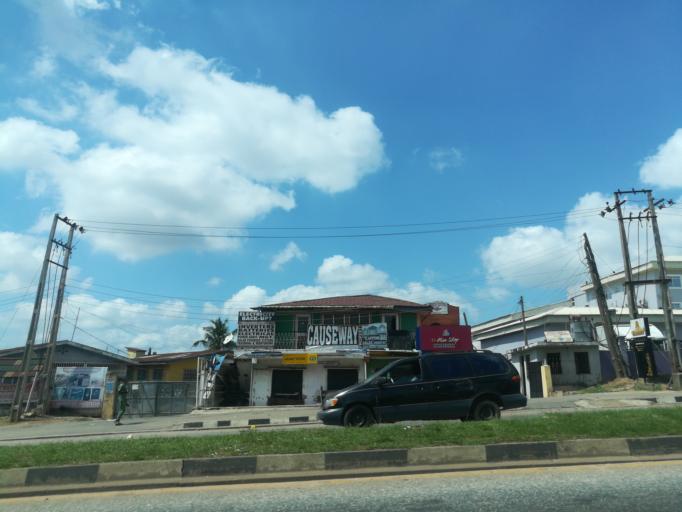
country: NG
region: Oyo
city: Ibadan
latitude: 7.3591
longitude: 3.8714
